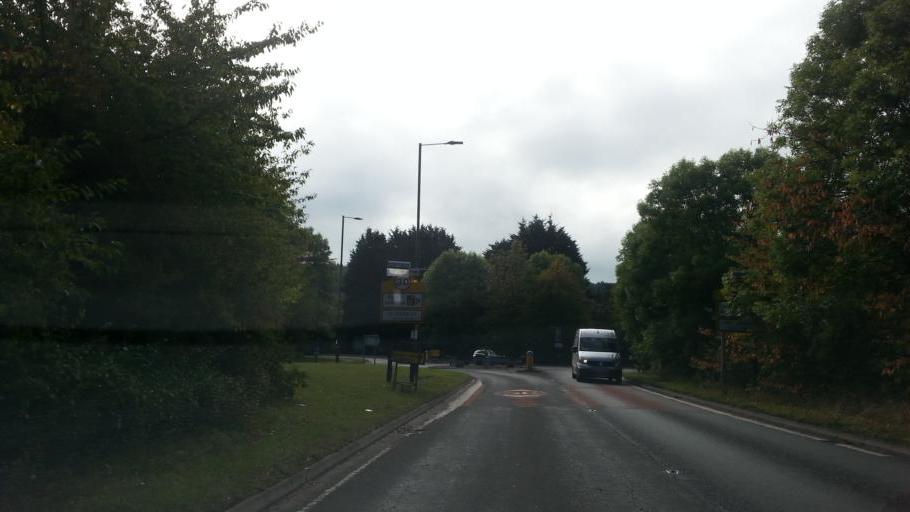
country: GB
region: England
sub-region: Herefordshire
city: Ross on Wye
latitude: 51.9152
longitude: -2.5700
